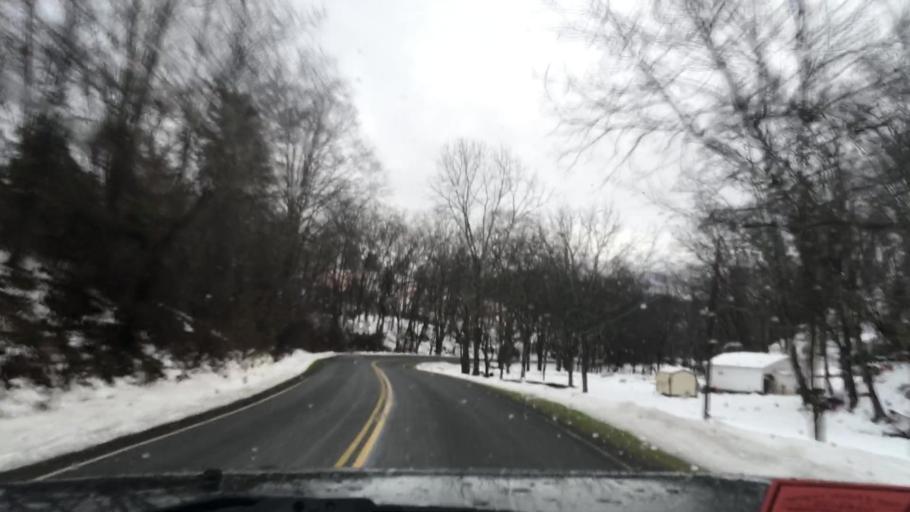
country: US
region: Virginia
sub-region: Pulaski County
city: Pulaski
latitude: 37.0120
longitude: -80.6953
